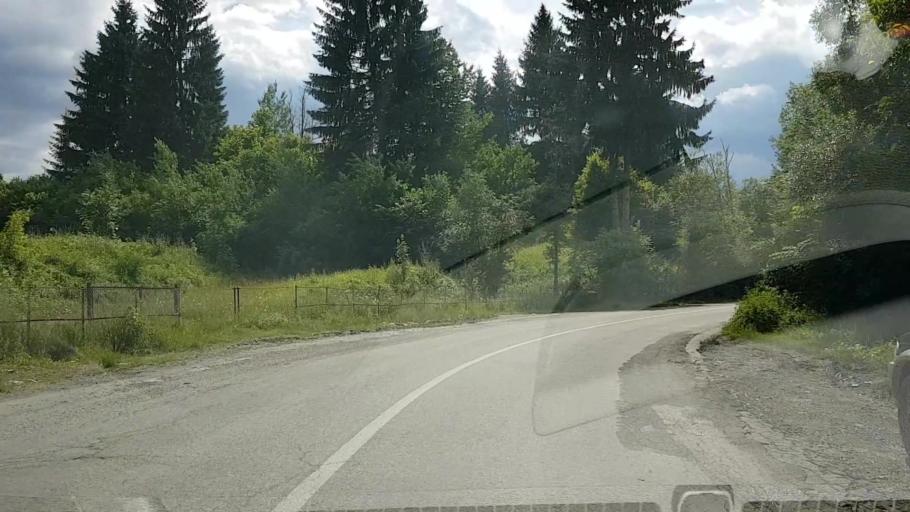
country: RO
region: Neamt
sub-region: Comuna Poiana Teiului
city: Poiana Teiului
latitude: 47.0822
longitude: 25.9696
